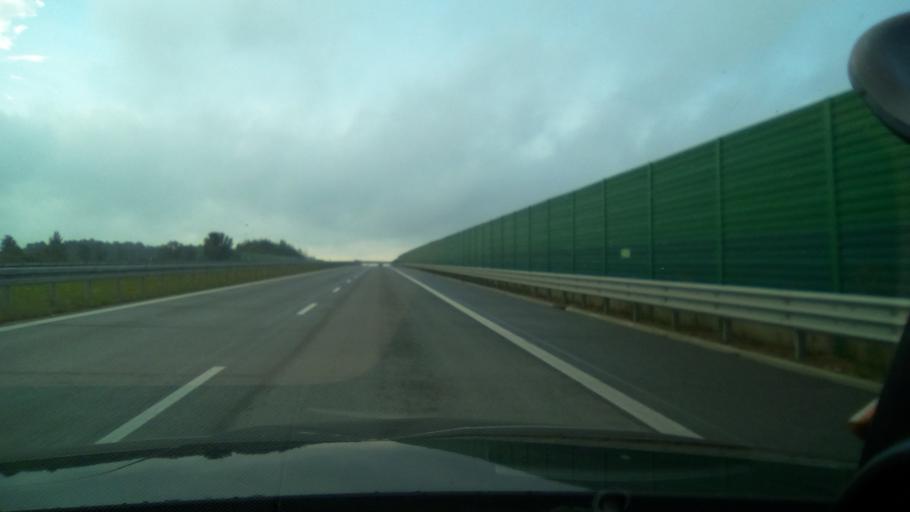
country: PL
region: Silesian Voivodeship
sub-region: Powiat czestochowski
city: Konopiska
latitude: 50.7677
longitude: 19.0151
